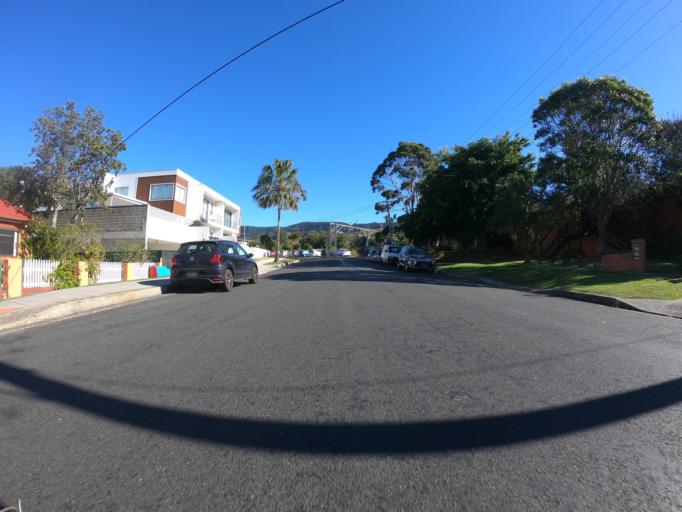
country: AU
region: New South Wales
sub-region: Wollongong
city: Bulli
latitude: -34.3142
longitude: 150.9224
